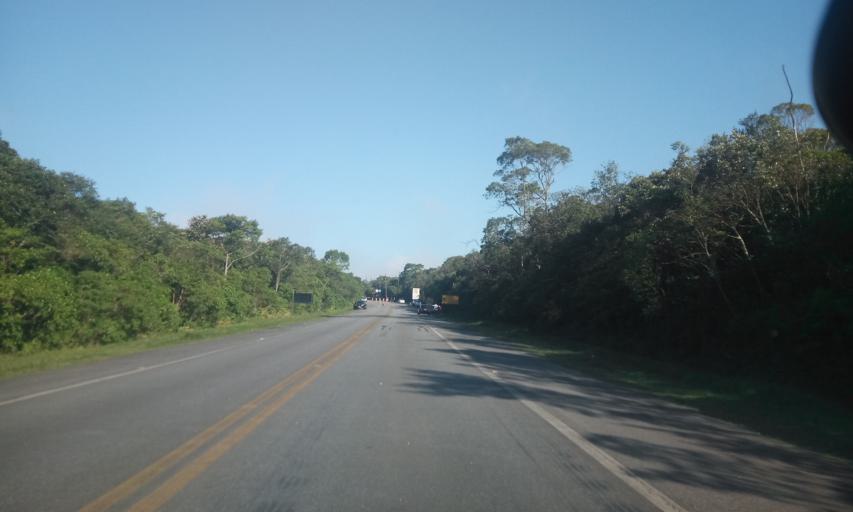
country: BR
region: Sao Paulo
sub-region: Cubatao
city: Cubatao
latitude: -23.8491
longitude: -46.4688
